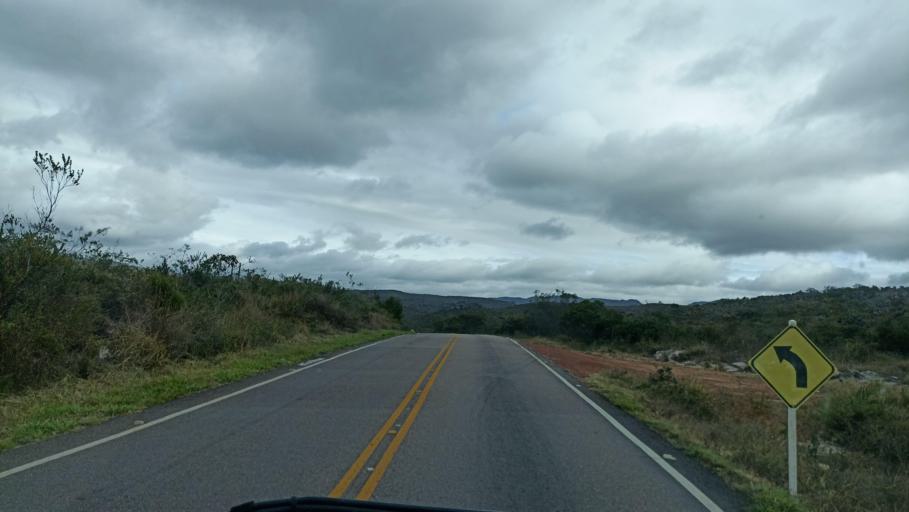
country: BR
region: Bahia
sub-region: Andarai
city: Vera Cruz
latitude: -12.9932
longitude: -41.3580
